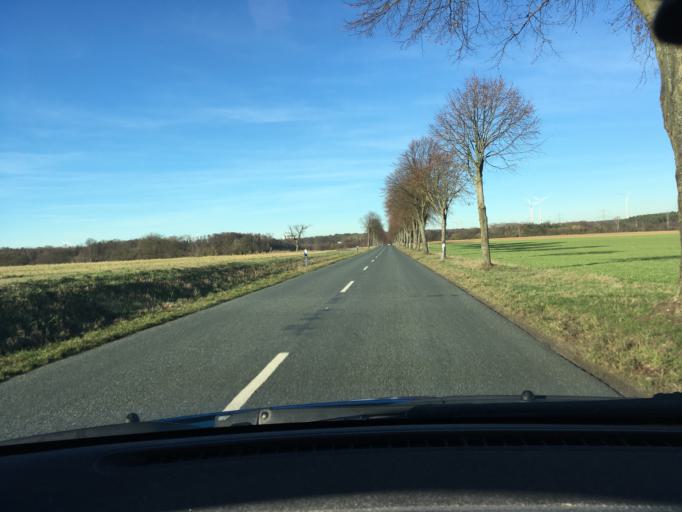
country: DE
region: Lower Saxony
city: Melbeck
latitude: 53.1627
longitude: 10.3832
